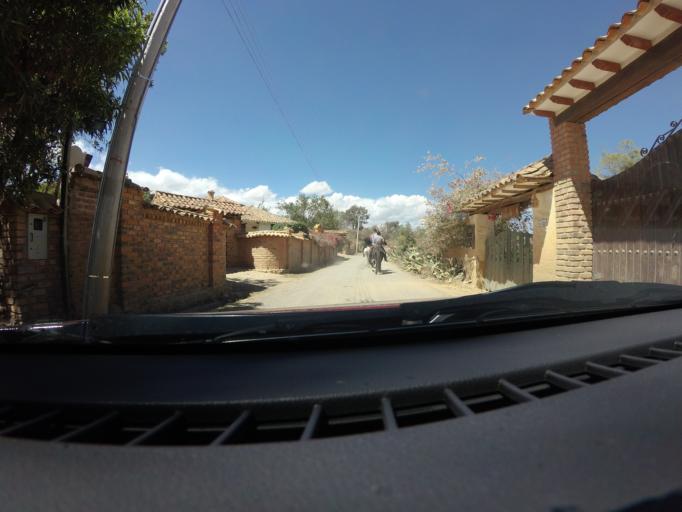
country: CO
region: Boyaca
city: Villa de Leiva
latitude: 5.6336
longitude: -73.5369
